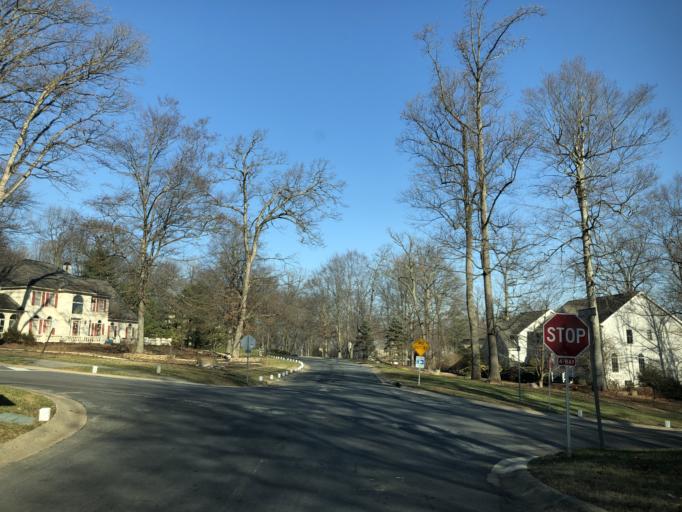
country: US
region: Pennsylvania
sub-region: Chester County
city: Downingtown
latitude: 39.9888
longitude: -75.7010
